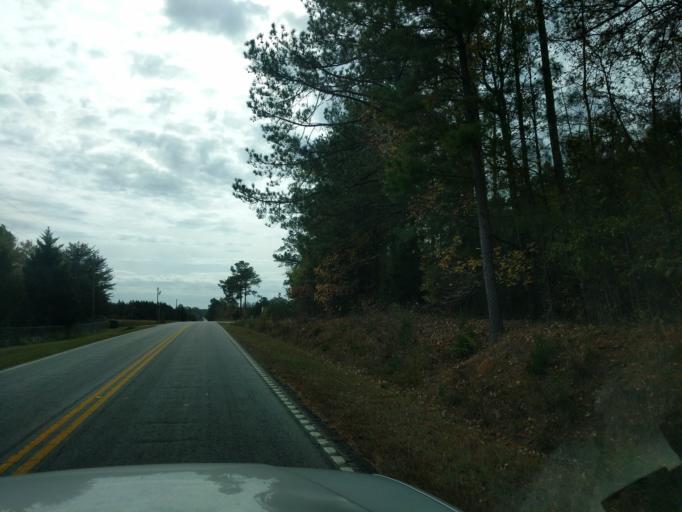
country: US
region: South Carolina
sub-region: Laurens County
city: Joanna
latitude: 34.3484
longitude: -81.8563
